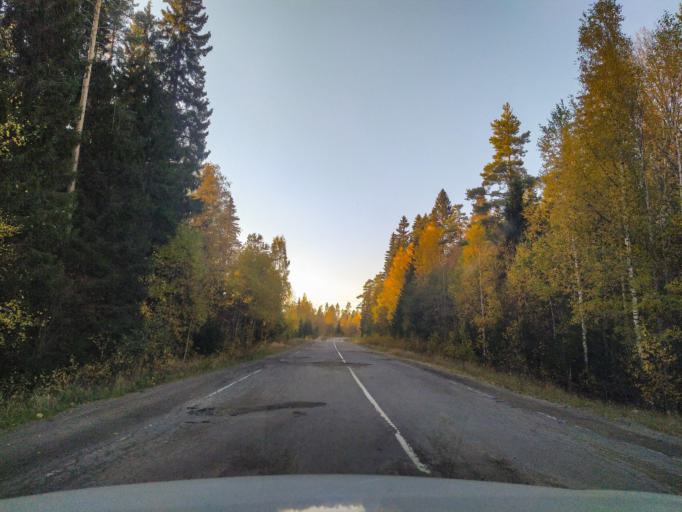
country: RU
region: Republic of Karelia
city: Lakhdenpokh'ya
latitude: 61.3699
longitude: 29.9823
